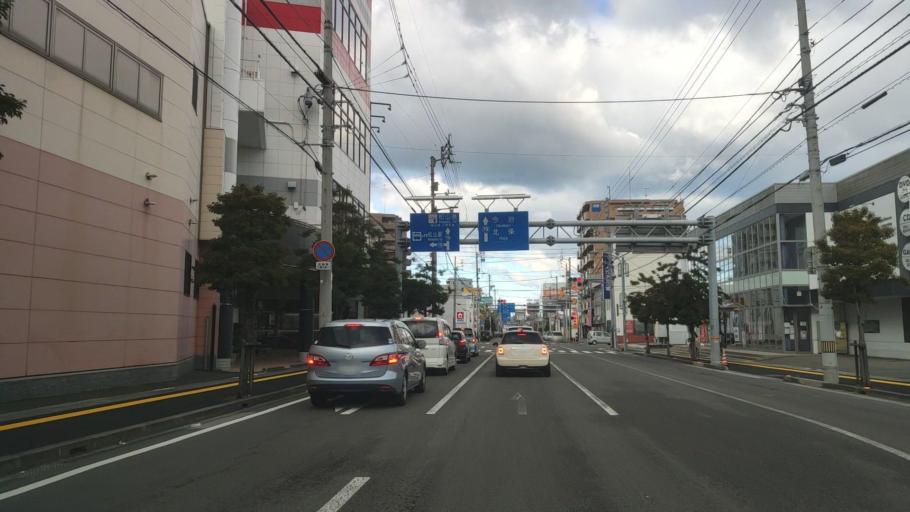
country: JP
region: Ehime
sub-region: Shikoku-chuo Shi
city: Matsuyama
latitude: 33.8540
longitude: 132.7530
